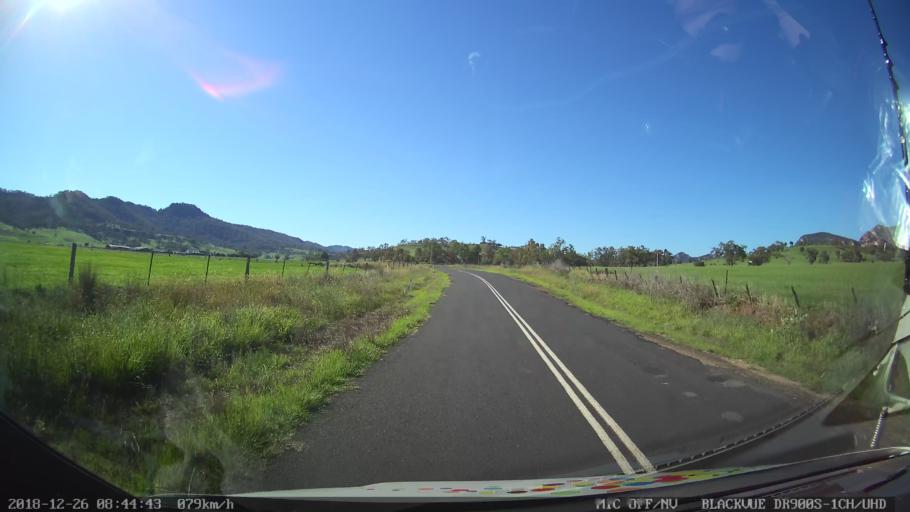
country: AU
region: New South Wales
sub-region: Mid-Western Regional
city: Kandos
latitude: -32.5178
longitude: 150.0812
